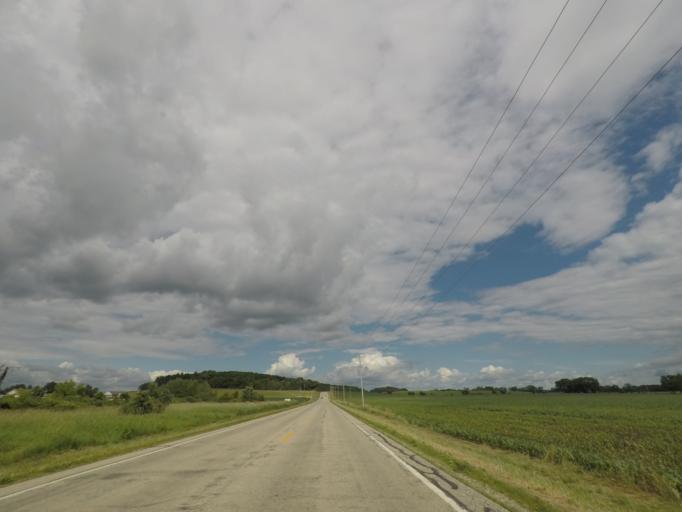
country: US
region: Wisconsin
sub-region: Dane County
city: Belleville
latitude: 42.8281
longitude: -89.4783
